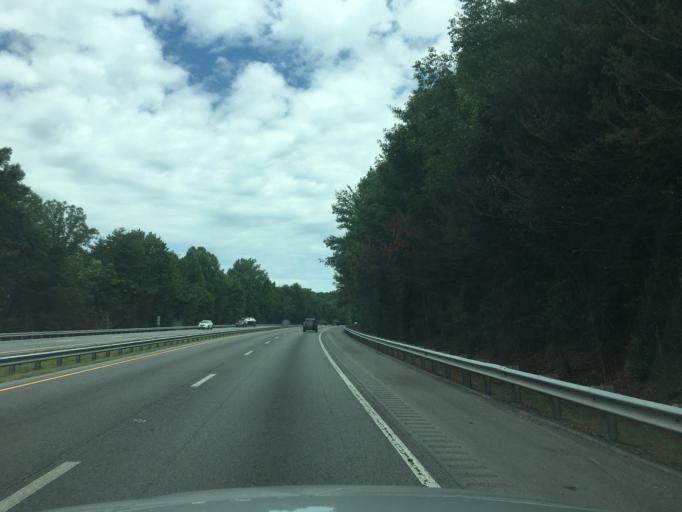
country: US
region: South Carolina
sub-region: Spartanburg County
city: Landrum
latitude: 35.2044
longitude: -82.1797
